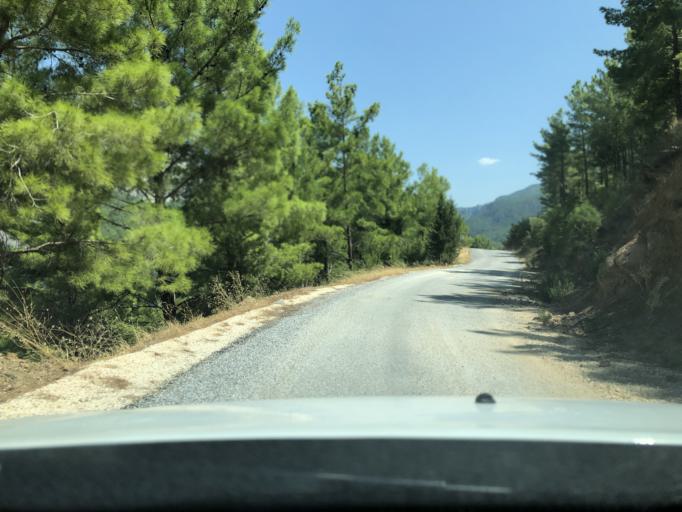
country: TR
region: Antalya
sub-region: Manavgat
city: Manavgat
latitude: 36.9119
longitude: 31.5466
